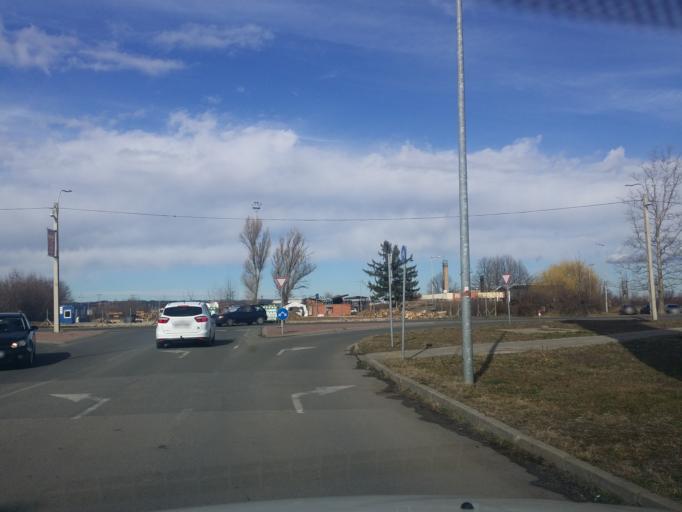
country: HU
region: Baranya
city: Mohacs
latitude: 45.9973
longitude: 18.6578
